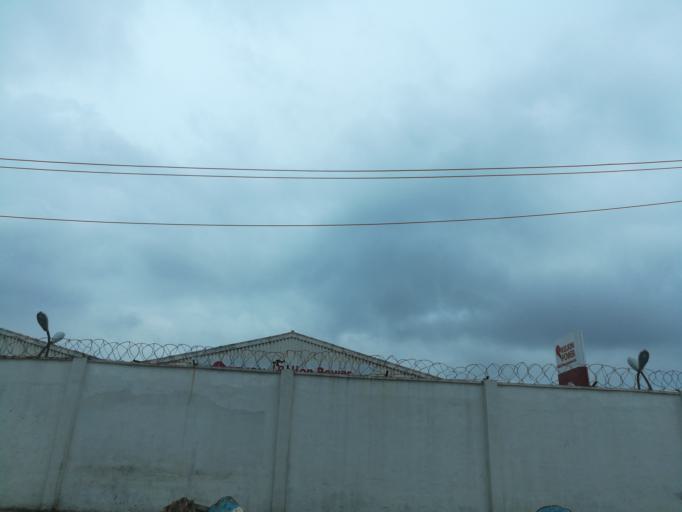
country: NG
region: Lagos
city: Ikeja
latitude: 6.6110
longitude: 3.3419
